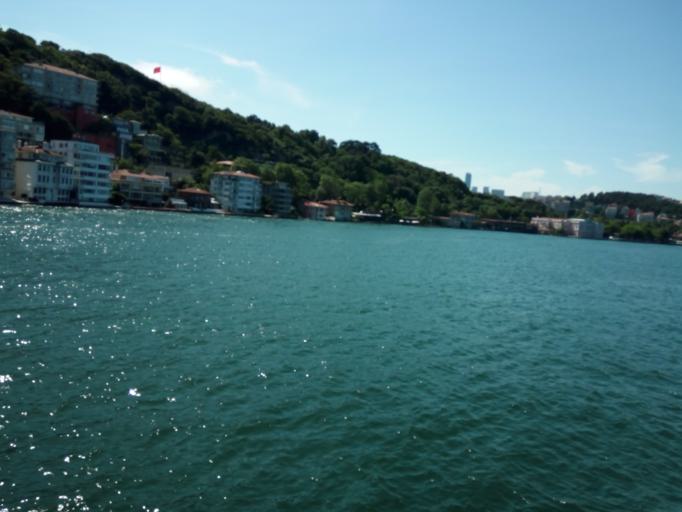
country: TR
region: Istanbul
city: UEskuedar
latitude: 41.0922
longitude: 29.0582
